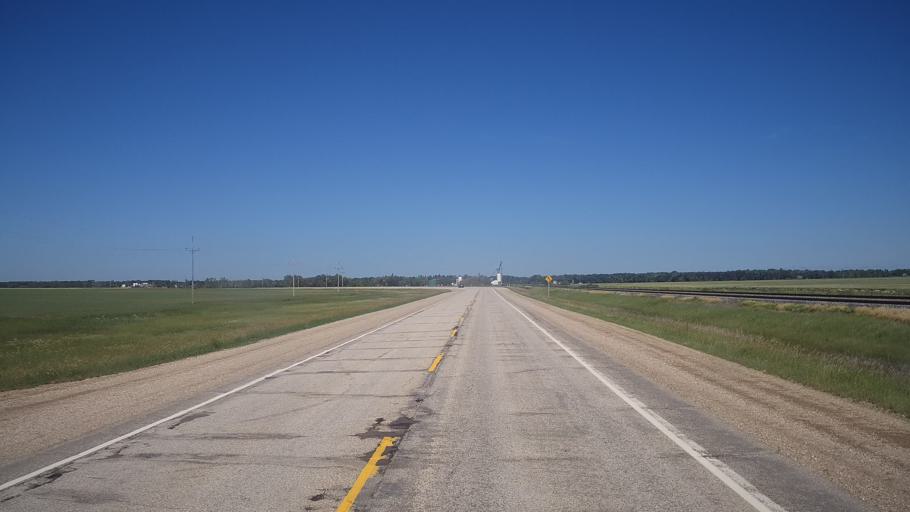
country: CA
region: Manitoba
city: Portage la Prairie
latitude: 50.1227
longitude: -98.5661
